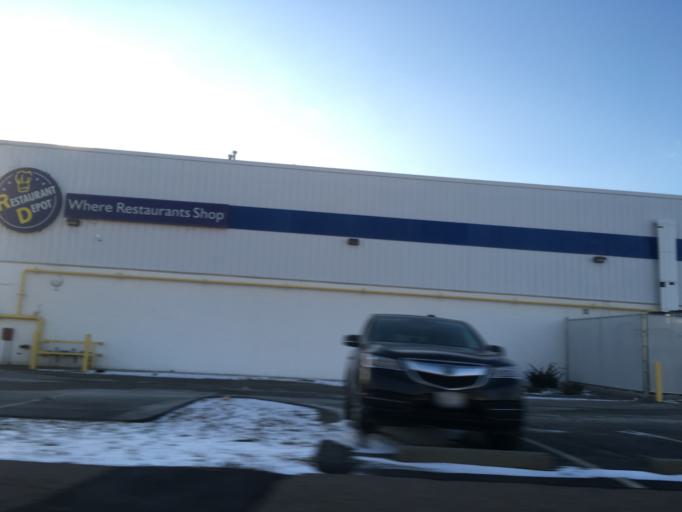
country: US
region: Rhode Island
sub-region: Providence County
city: Cranston
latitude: 41.7947
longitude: -71.4388
